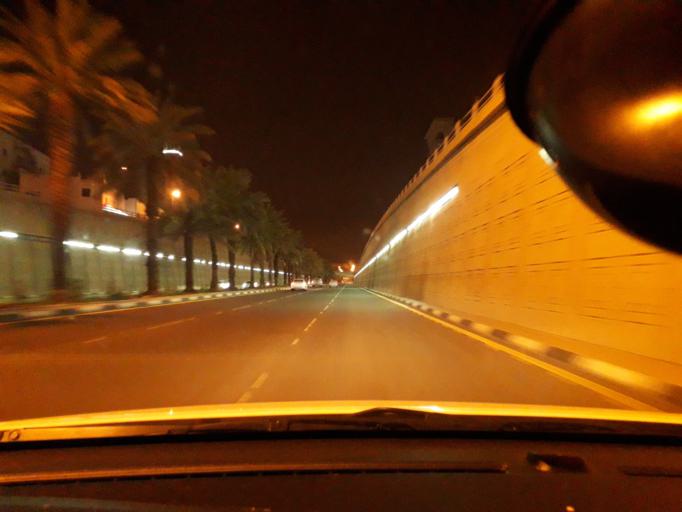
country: SA
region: Al Madinah al Munawwarah
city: Sultanah
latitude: 24.4673
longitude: 39.5872
